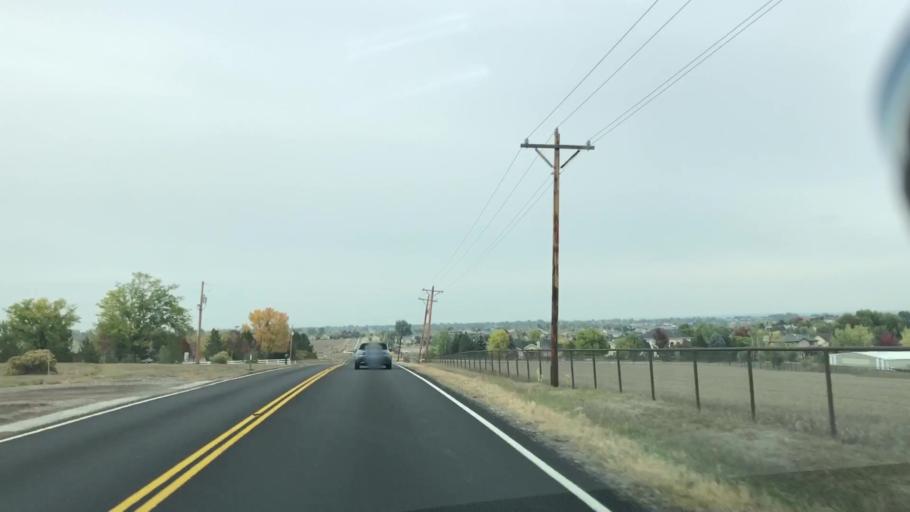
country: US
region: Colorado
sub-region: Larimer County
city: Loveland
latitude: 40.4747
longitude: -105.0583
